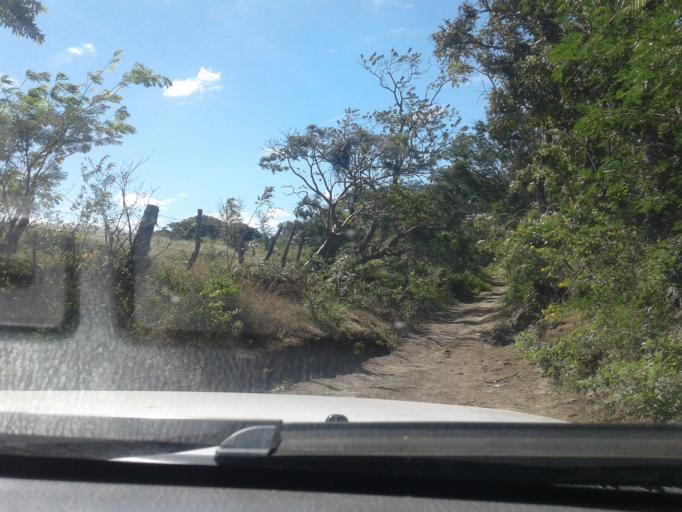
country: NI
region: Carazo
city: Santa Teresa
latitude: 11.7756
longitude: -86.1875
